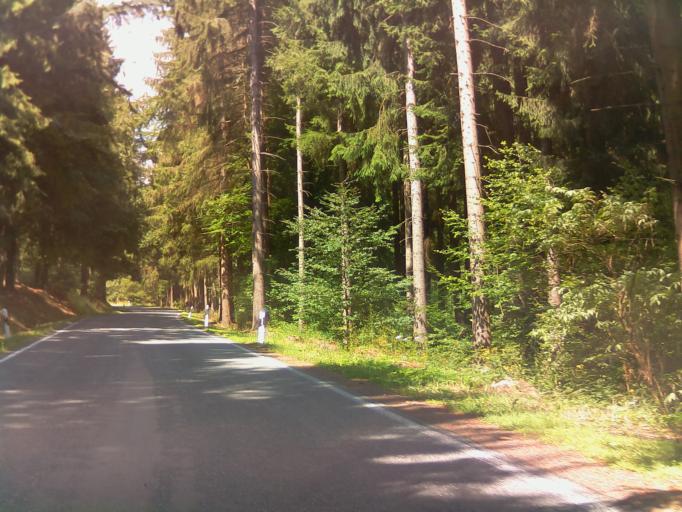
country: DE
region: Thuringia
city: Neustadt am Rennsteig
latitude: 50.5596
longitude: 10.9421
